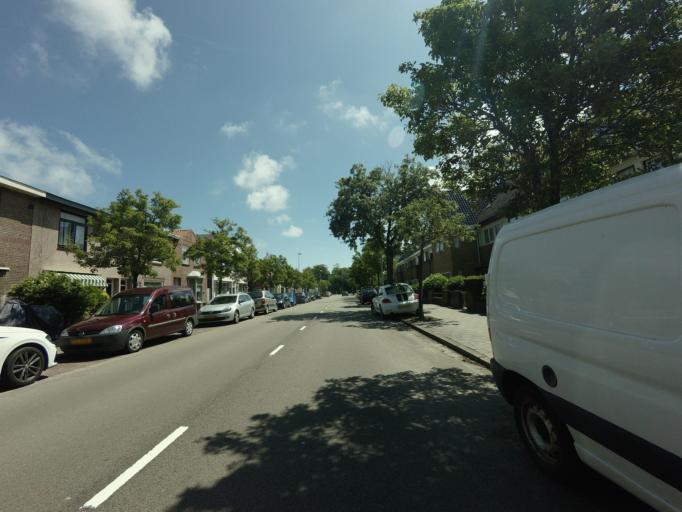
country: NL
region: North Holland
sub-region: Gemeente Den Helder
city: Den Helder
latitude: 52.9527
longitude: 4.7701
